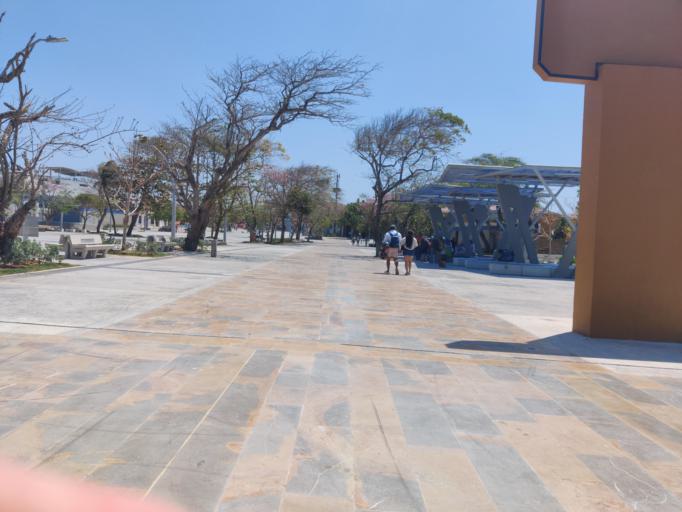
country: CO
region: Atlantico
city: Puerto Colombia
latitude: 10.9888
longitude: -74.9602
